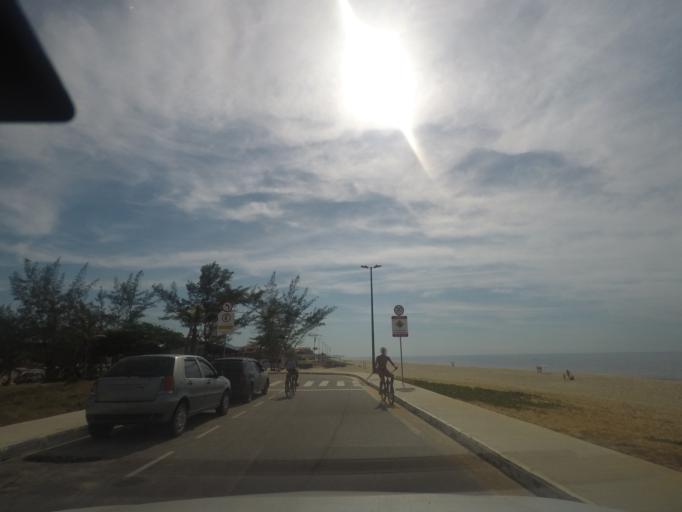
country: BR
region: Rio de Janeiro
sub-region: Marica
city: Marica
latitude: -22.9612
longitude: -42.8177
